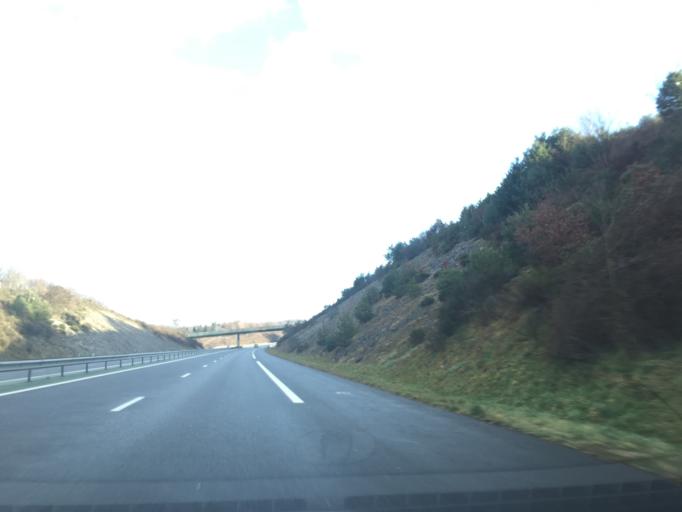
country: FR
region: Limousin
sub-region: Departement de la Correze
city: Saint-Mexant
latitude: 45.2978
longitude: 1.6469
